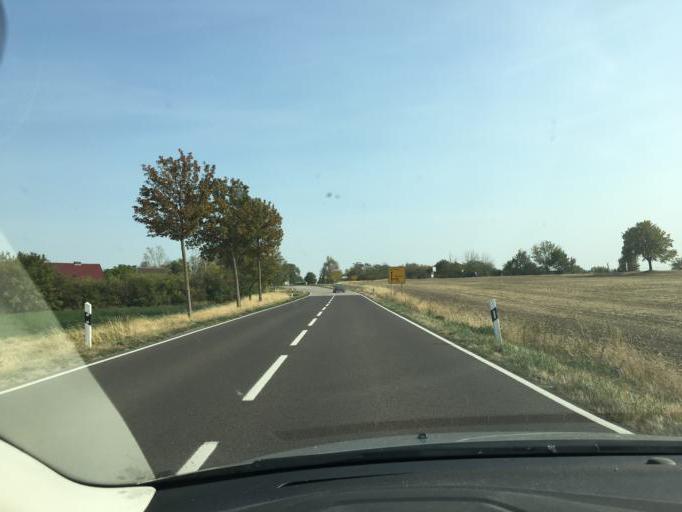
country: DE
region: Saxony-Anhalt
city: Wulfen
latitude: 51.7748
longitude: 11.9052
